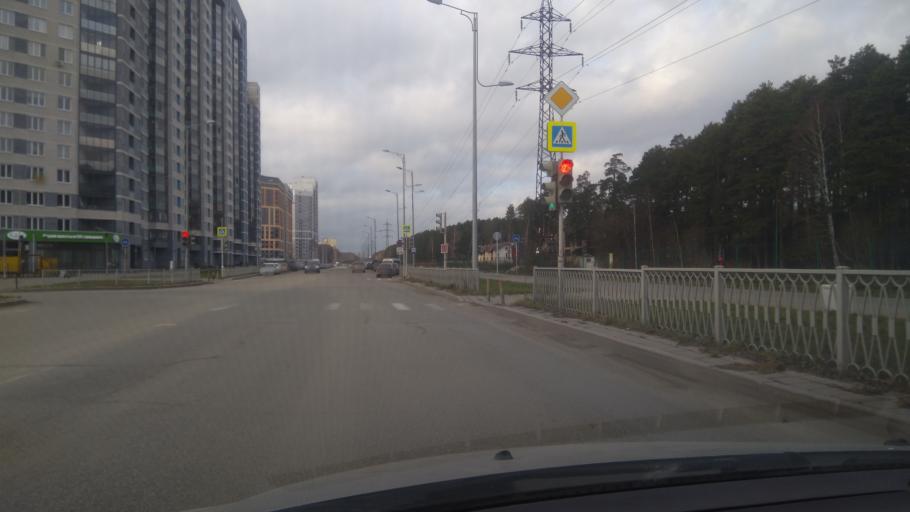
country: RU
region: Sverdlovsk
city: Sovkhoznyy
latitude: 56.7823
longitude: 60.5551
